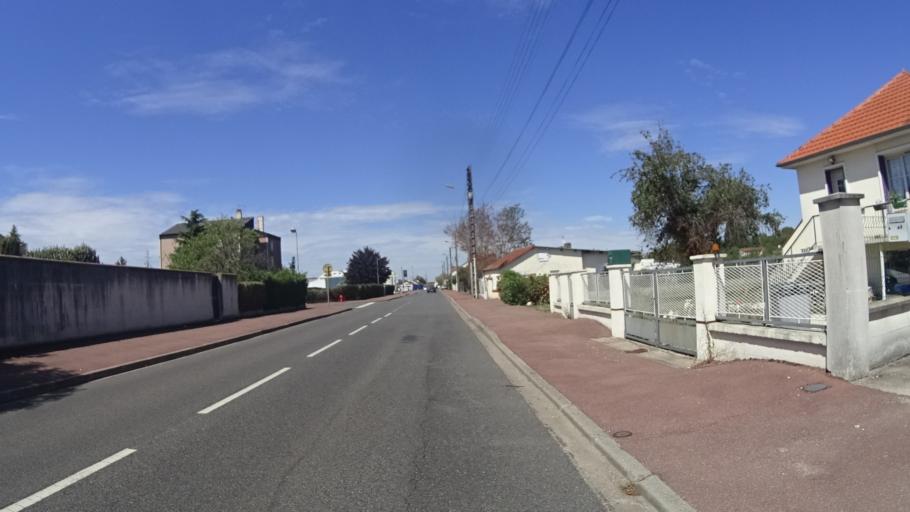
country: FR
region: Centre
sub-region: Departement du Loiret
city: Briare
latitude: 47.6277
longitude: 2.7484
